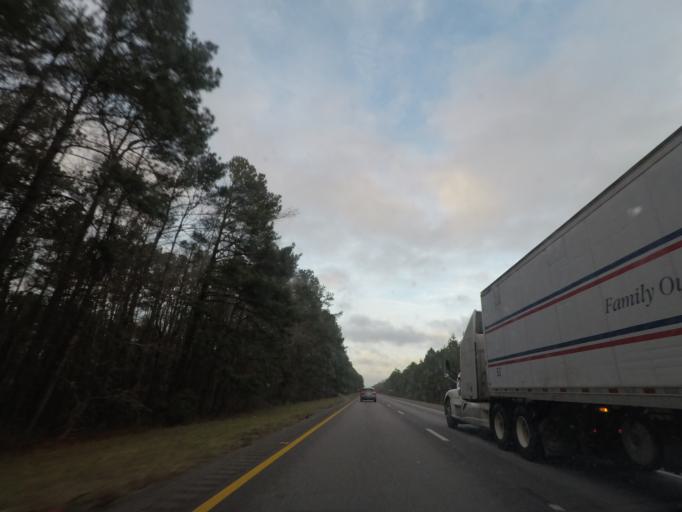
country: US
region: South Carolina
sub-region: Orangeburg County
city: Holly Hill
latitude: 33.3320
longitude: -80.5389
